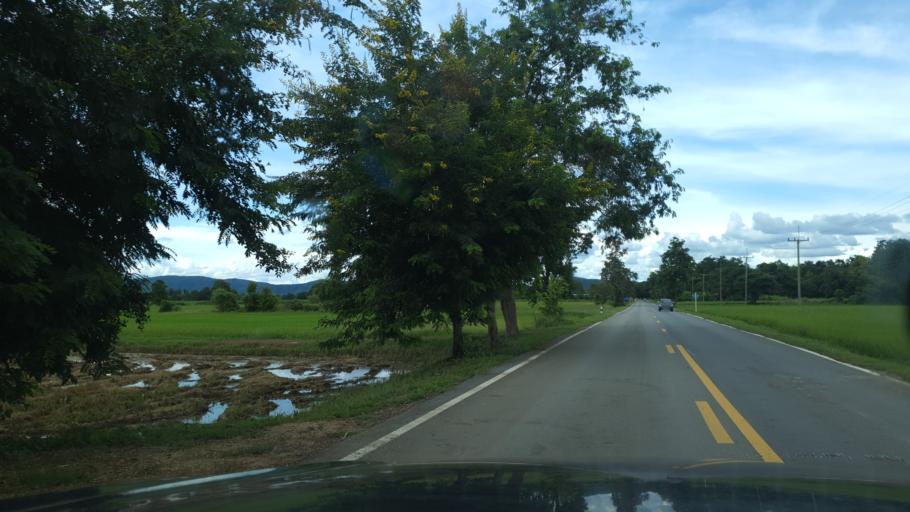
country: TH
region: Sukhothai
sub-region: Amphoe Si Satchanalai
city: Si Satchanalai
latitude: 17.4709
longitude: 99.7549
